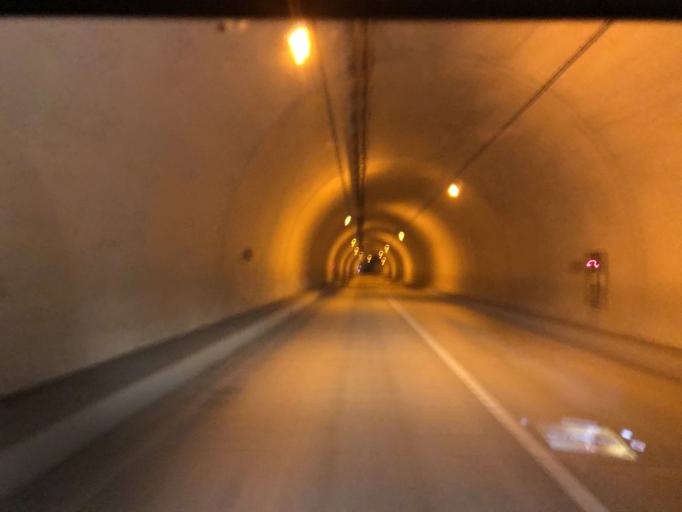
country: JP
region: Iwate
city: Ichinoseki
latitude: 38.8234
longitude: 141.3164
